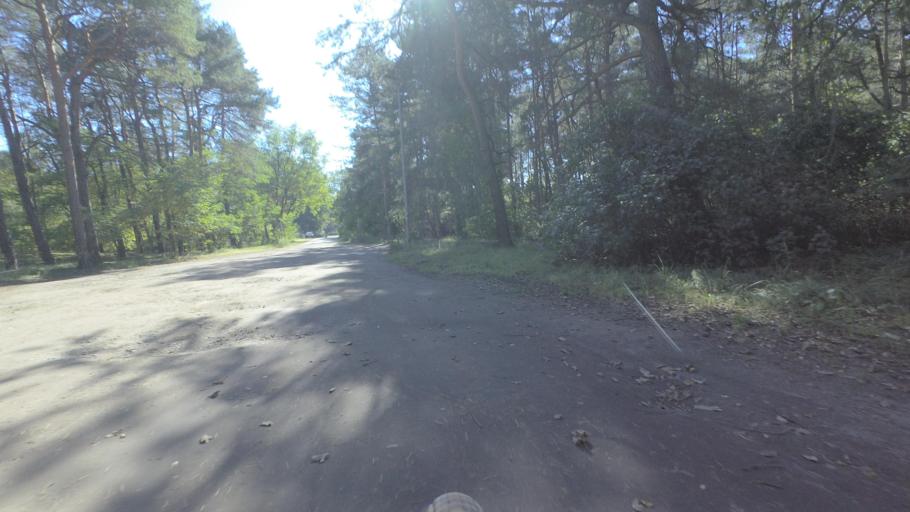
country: DE
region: Brandenburg
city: Am Mellensee
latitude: 52.1886
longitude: 13.3992
